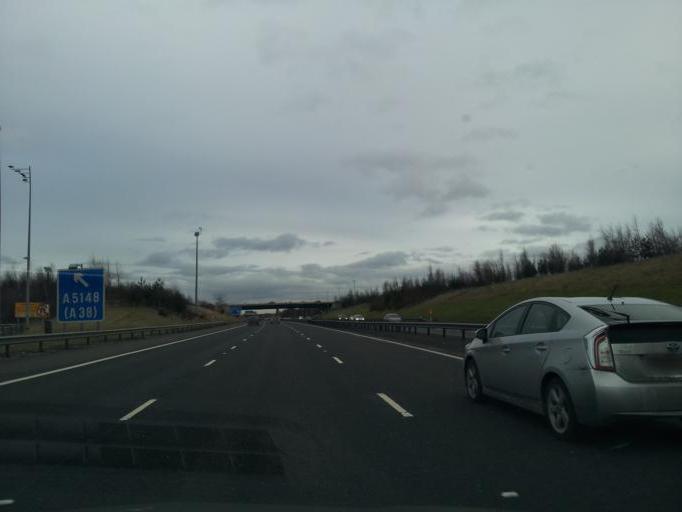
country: GB
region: England
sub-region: Staffordshire
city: Shenstone
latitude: 52.6490
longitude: -1.8383
